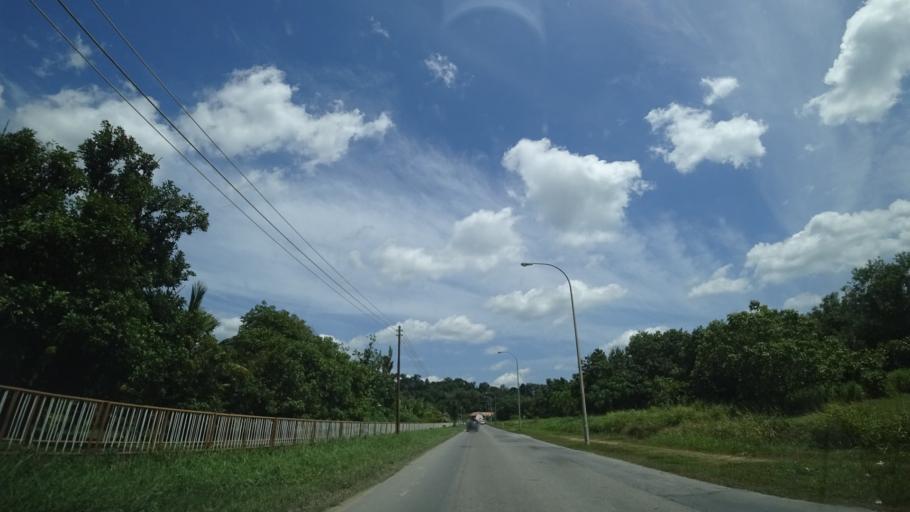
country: BN
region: Brunei and Muara
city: Bandar Seri Begawan
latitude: 4.8691
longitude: 114.8597
